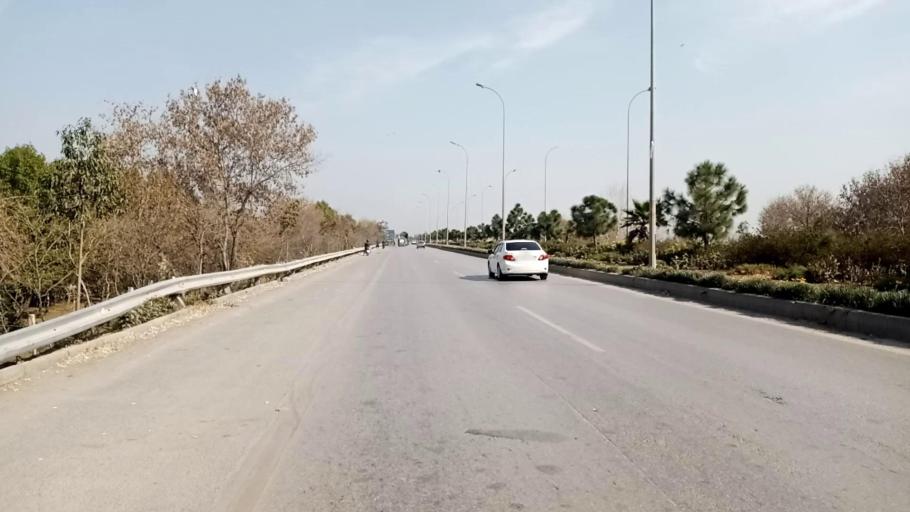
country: PK
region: Khyber Pakhtunkhwa
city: Peshawar
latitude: 34.0255
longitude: 71.6347
